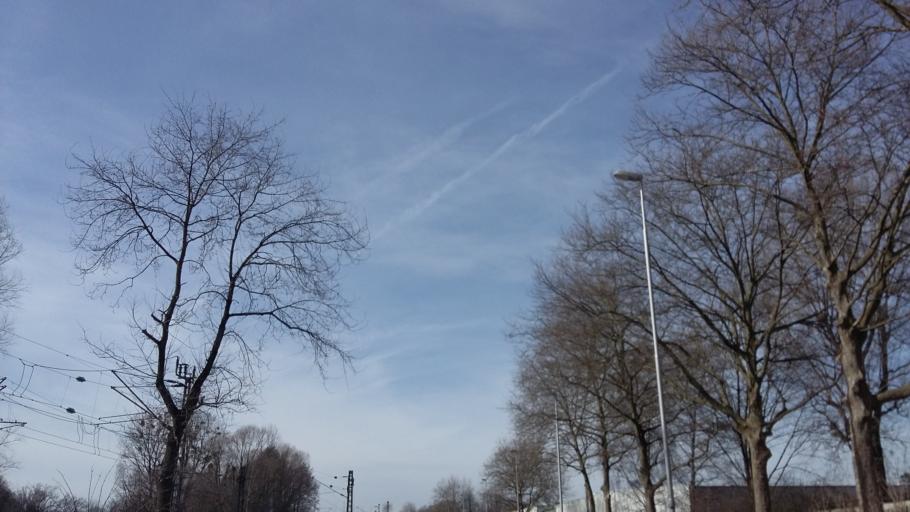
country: AT
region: Vorarlberg
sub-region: Politischer Bezirk Bregenz
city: Horbranz
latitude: 47.5513
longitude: 9.7179
